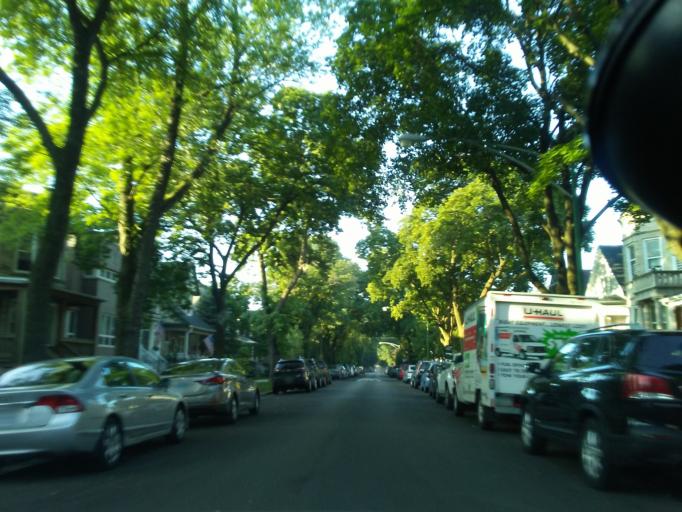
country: US
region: Illinois
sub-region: Cook County
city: Lincolnwood
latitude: 41.9300
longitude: -87.7159
